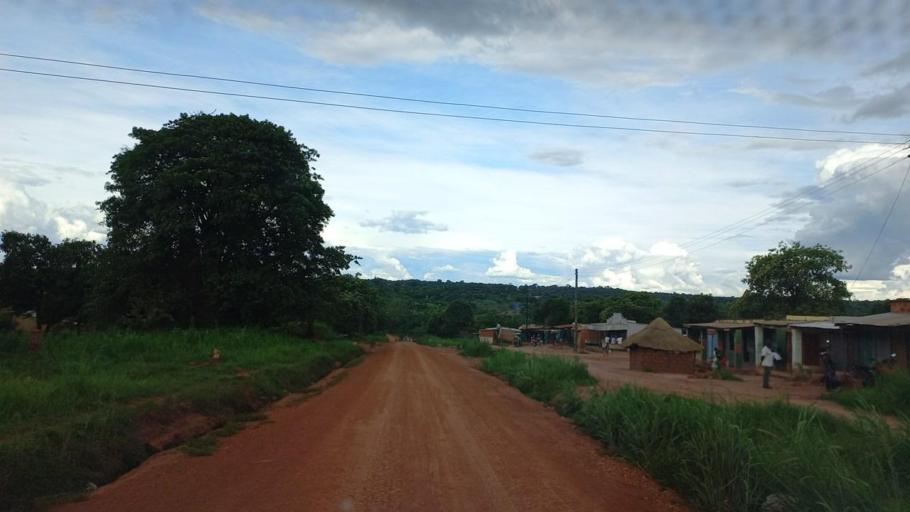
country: ZM
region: North-Western
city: Mwinilunga
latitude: -11.7558
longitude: 24.4339
